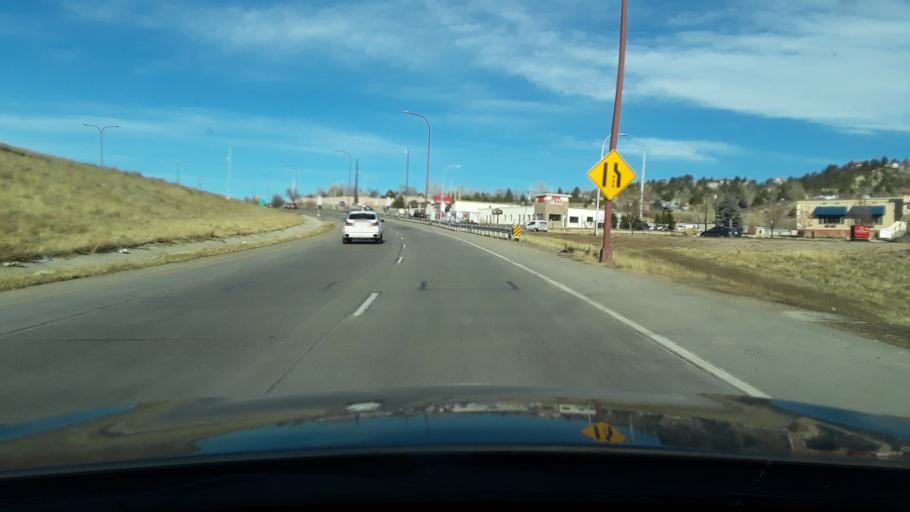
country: US
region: Colorado
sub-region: El Paso County
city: Colorado Springs
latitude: 38.9162
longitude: -104.8156
